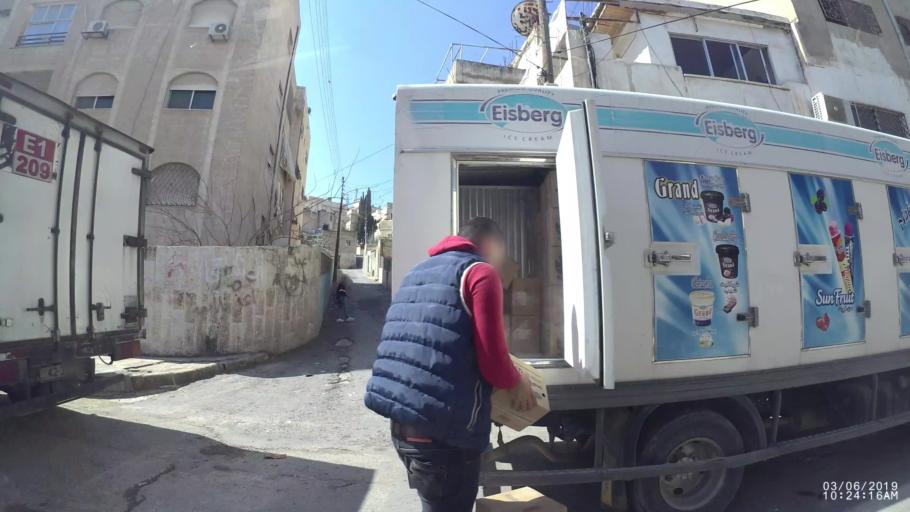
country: JO
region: Amman
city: Amman
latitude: 31.9824
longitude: 35.9822
